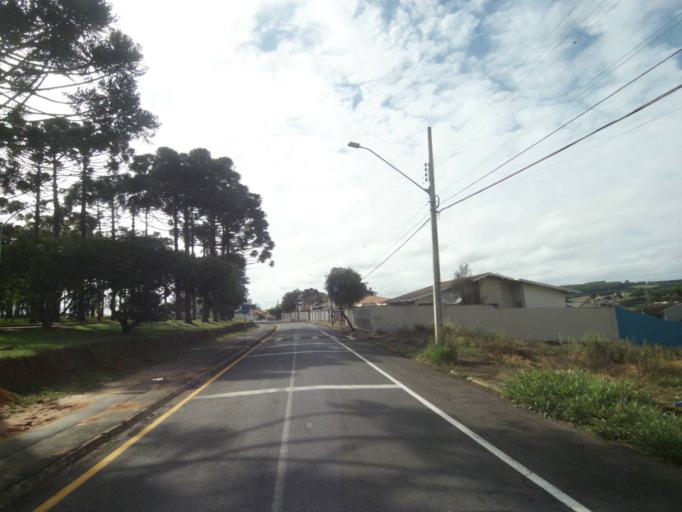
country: BR
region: Parana
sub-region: Telemaco Borba
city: Telemaco Borba
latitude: -24.3326
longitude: -50.6099
